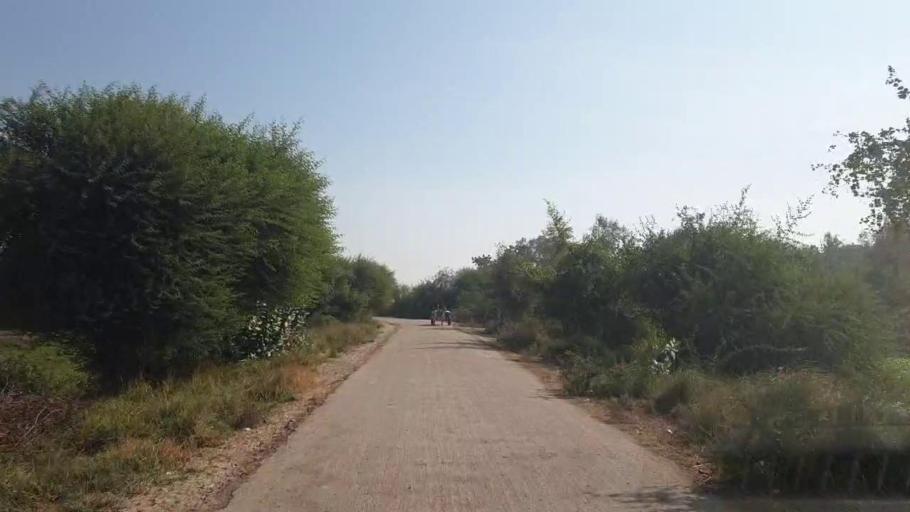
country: PK
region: Sindh
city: Matiari
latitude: 25.6760
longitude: 68.3567
